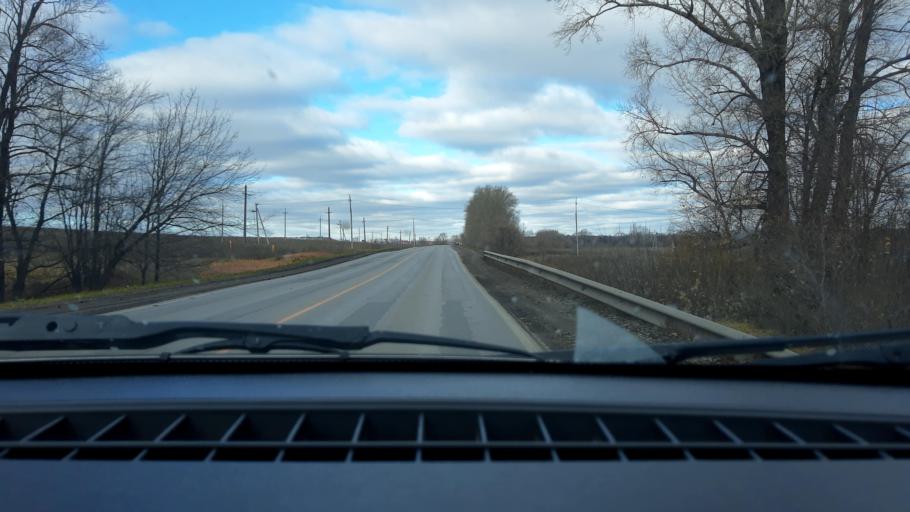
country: RU
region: Bashkortostan
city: Avdon
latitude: 54.7255
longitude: 55.8066
